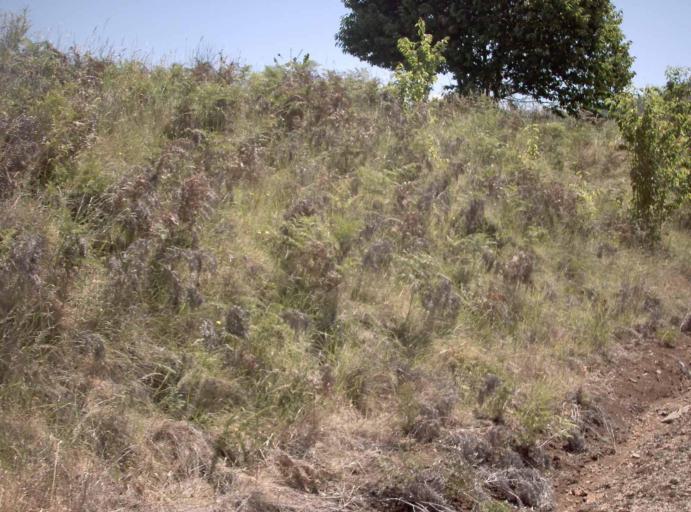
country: AU
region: Victoria
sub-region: East Gippsland
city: Lakes Entrance
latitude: -37.3968
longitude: 148.2142
